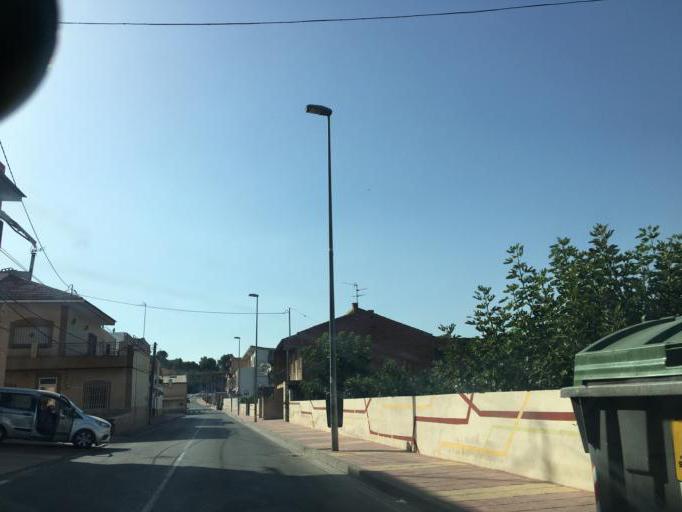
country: ES
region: Murcia
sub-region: Murcia
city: Santomera
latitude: 38.0385
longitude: -1.0808
